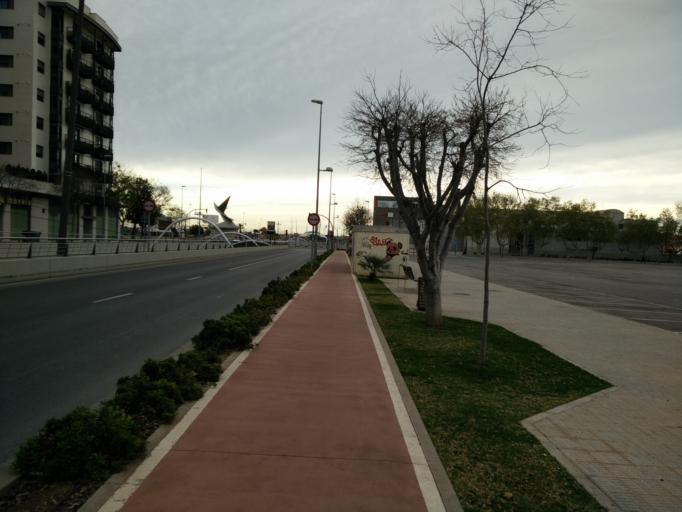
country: ES
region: Valencia
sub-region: Provincia de Castello
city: Castello de la Plana
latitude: 39.9840
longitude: -0.0264
